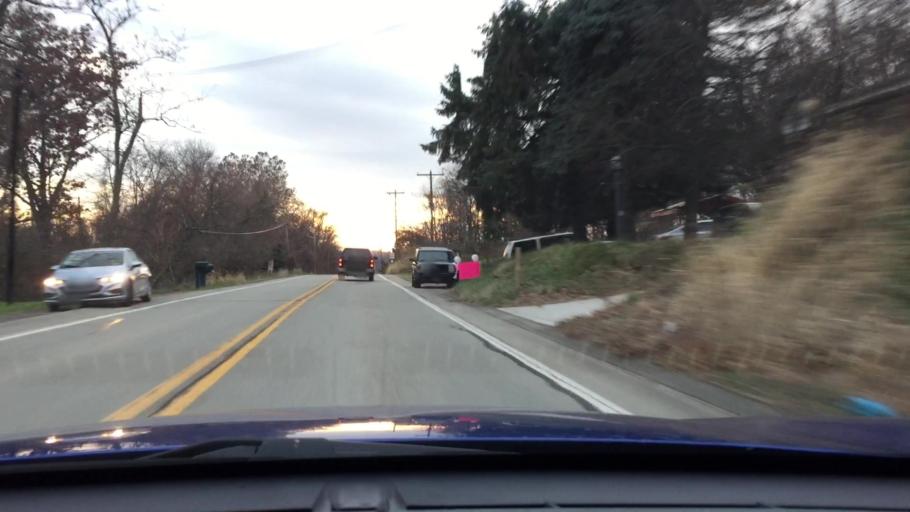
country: US
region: Pennsylvania
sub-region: Allegheny County
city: Elizabeth
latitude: 40.2507
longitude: -79.8548
